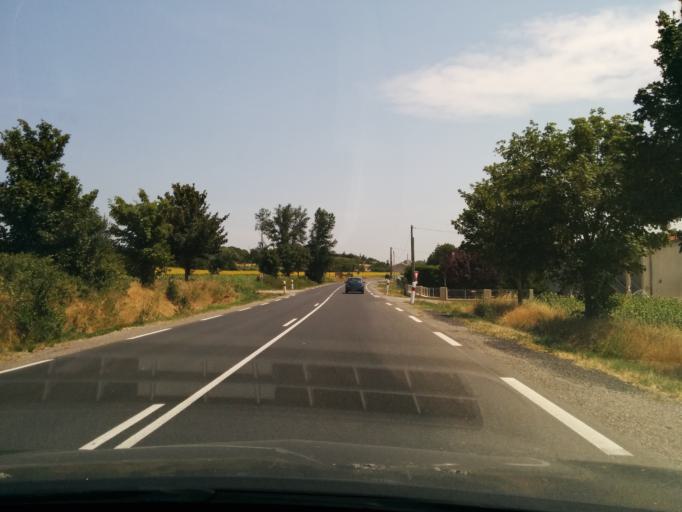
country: FR
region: Midi-Pyrenees
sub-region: Departement de la Haute-Garonne
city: Avignonet-Lauragais
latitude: 43.3584
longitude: 1.8166
